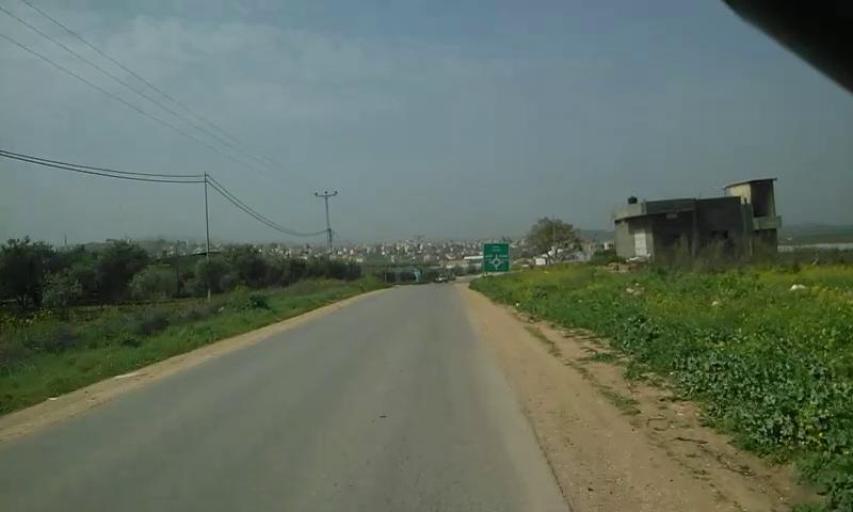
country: PS
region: West Bank
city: Silat al Harithiyah
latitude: 32.5017
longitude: 35.2447
